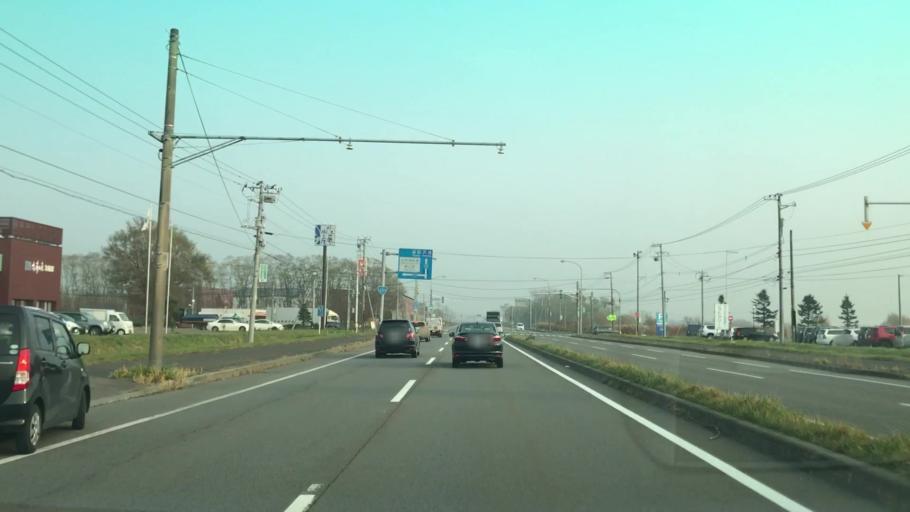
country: JP
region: Hokkaido
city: Ishikari
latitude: 43.2072
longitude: 141.3327
